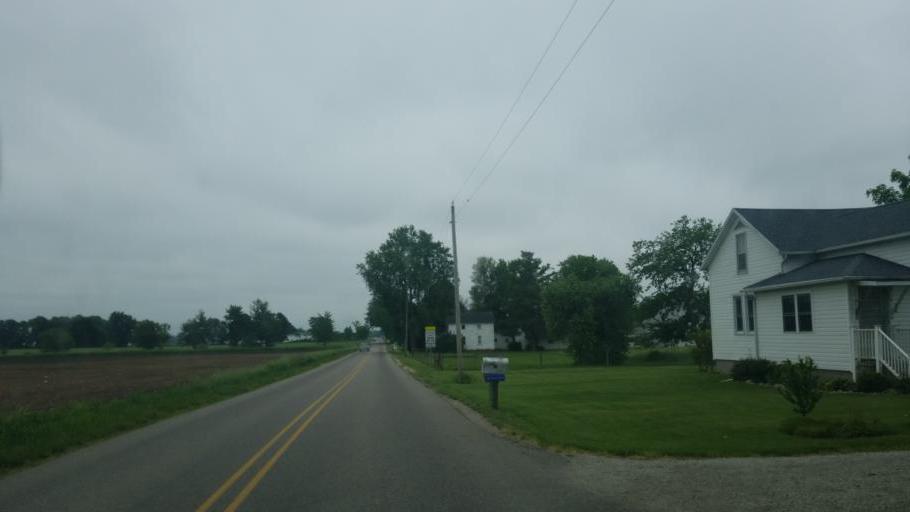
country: US
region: Indiana
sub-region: Elkhart County
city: Nappanee
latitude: 41.4696
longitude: -86.0208
